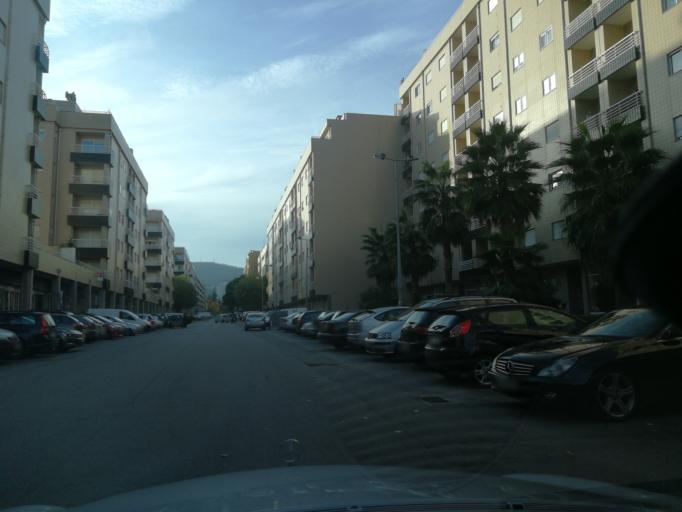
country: PT
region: Braga
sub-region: Braga
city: Braga
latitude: 41.5466
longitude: -8.4056
